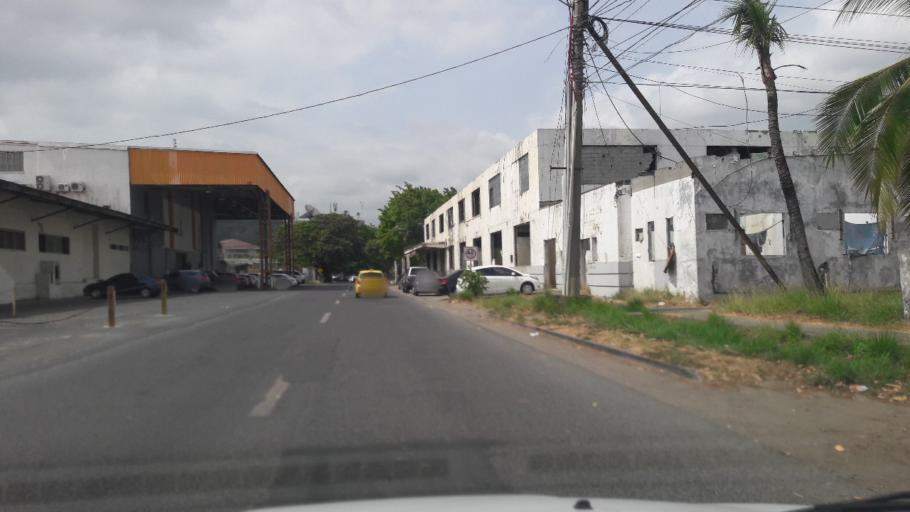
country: PA
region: Panama
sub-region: Distrito de Panama
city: Ancon
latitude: 8.9723
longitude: -79.5477
